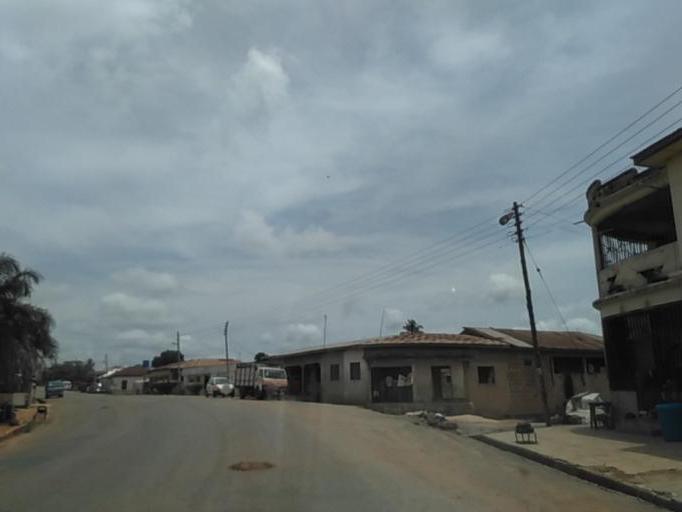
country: GH
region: Ashanti
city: Mamponteng
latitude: 6.8282
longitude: -1.4966
